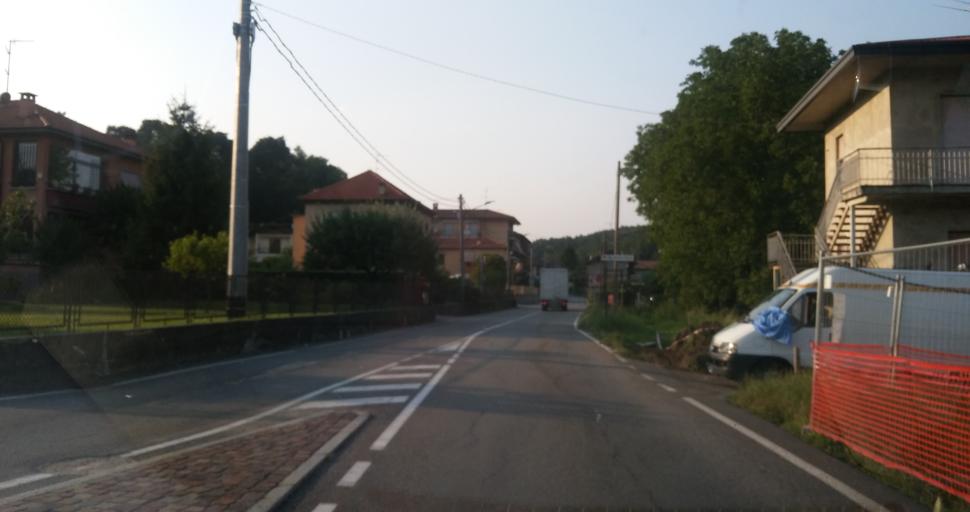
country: IT
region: Lombardy
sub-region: Provincia di Varese
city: Vergiate
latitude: 45.7234
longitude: 8.6893
